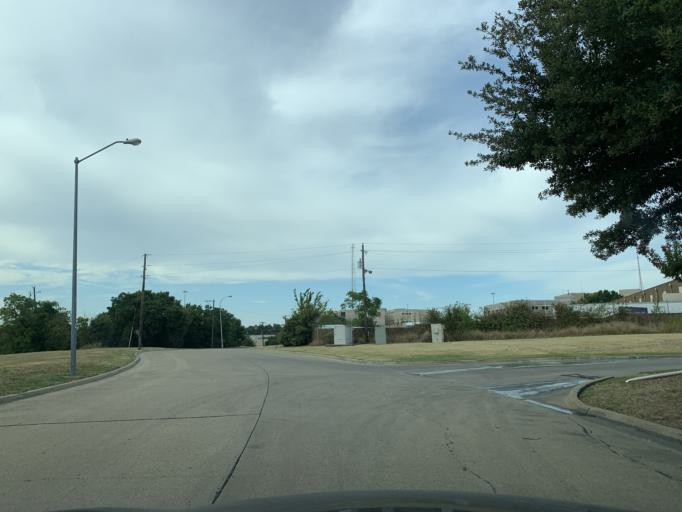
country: US
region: Texas
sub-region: Dallas County
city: Cockrell Hill
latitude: 32.7711
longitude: -96.8662
